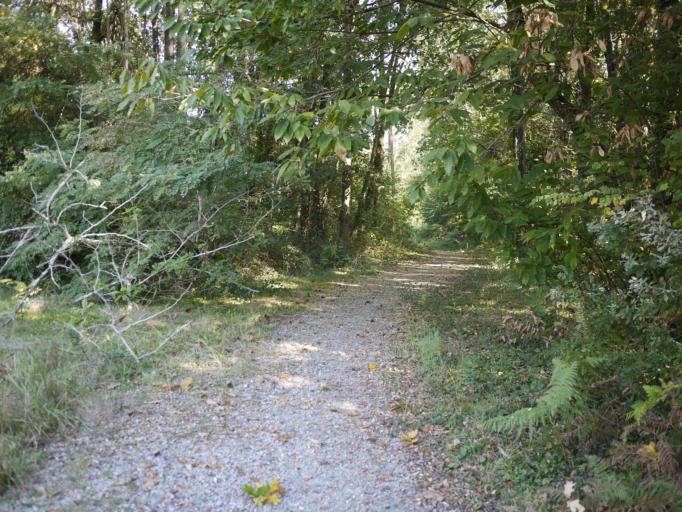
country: FR
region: Aquitaine
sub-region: Departement des Landes
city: Saint-Paul-les-Dax
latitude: 43.7235
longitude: -1.0779
